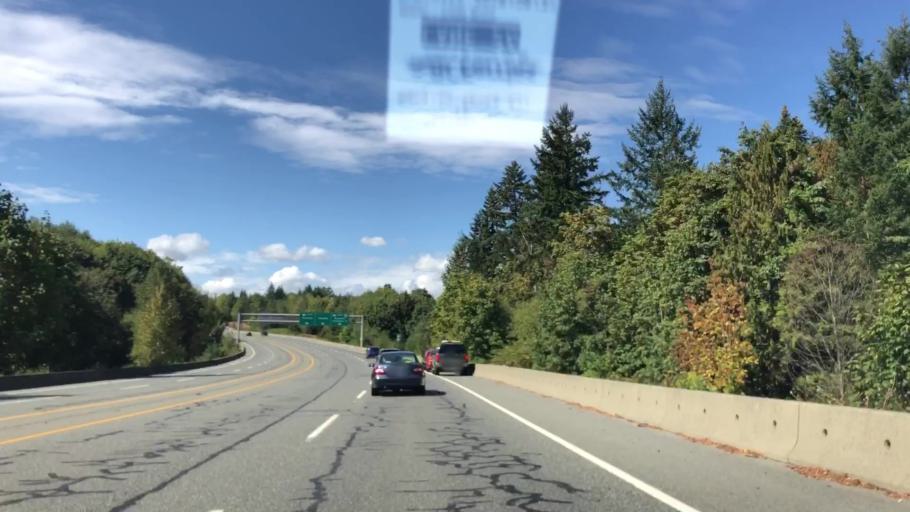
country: CA
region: British Columbia
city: Nanaimo
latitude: 49.1138
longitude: -123.8870
